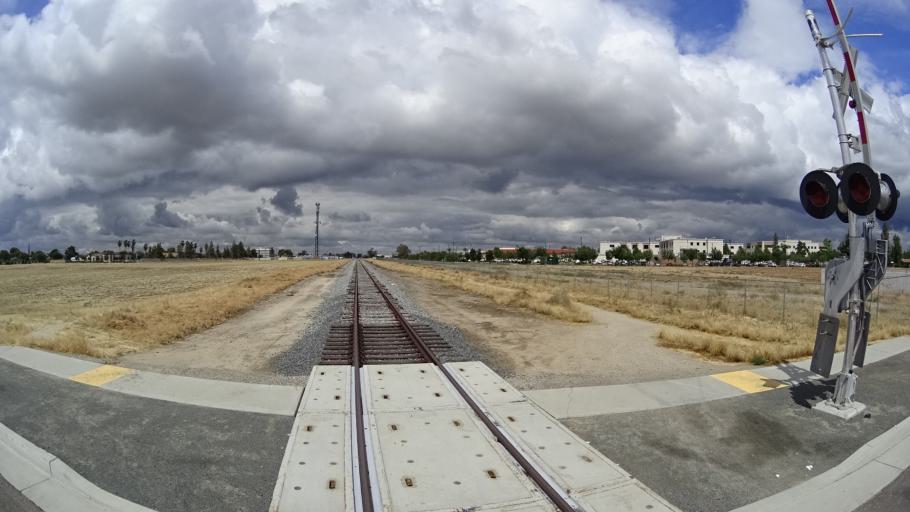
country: US
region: California
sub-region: Kings County
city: Hanford
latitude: 36.3222
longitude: -119.6641
